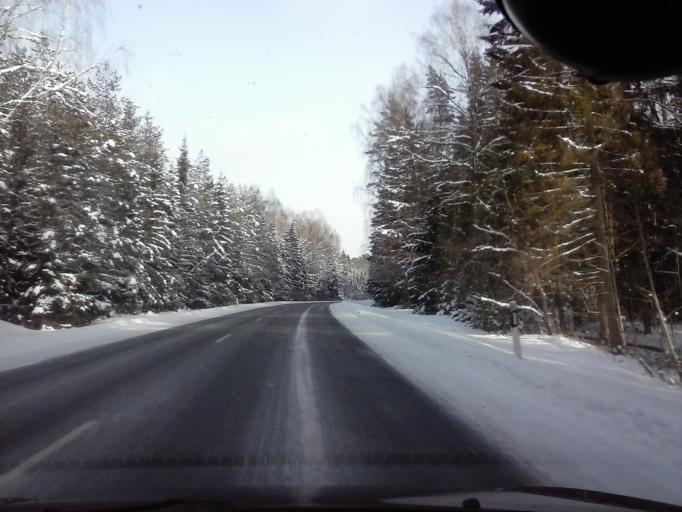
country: EE
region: Viljandimaa
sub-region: Moisakuela linn
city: Moisakula
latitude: 58.2568
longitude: 25.2068
